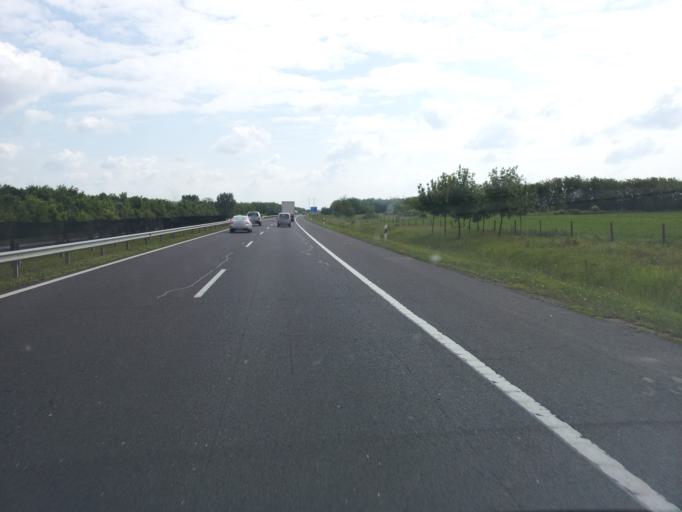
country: HU
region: Borsod-Abauj-Zemplen
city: Emod
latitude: 47.8811
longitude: 20.8339
